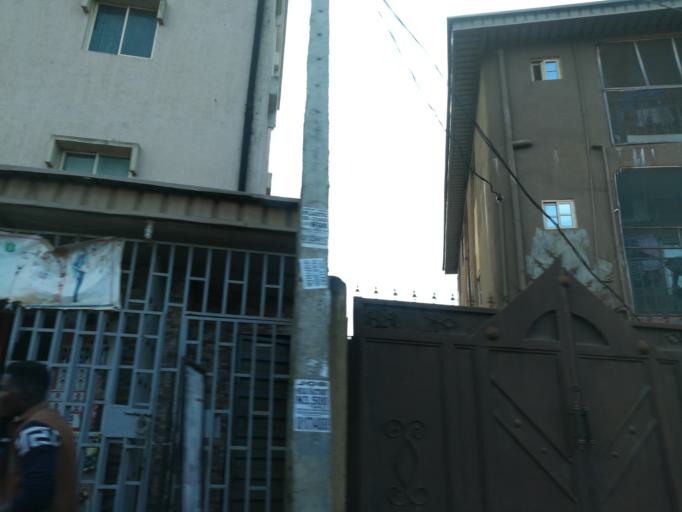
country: NG
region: Lagos
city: Oshodi
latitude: 6.5530
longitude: 3.3316
